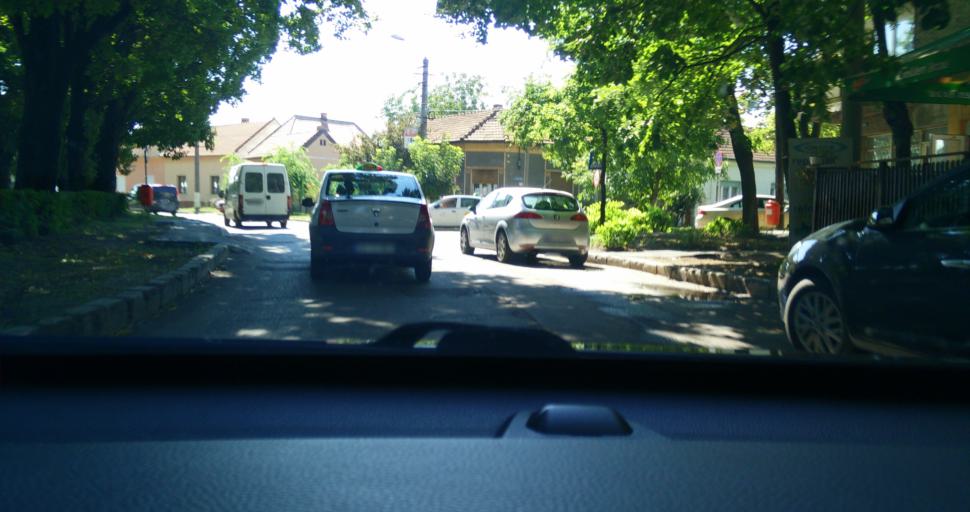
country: RO
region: Bihor
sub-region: Comuna Biharea
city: Oradea
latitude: 47.0431
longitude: 21.9336
